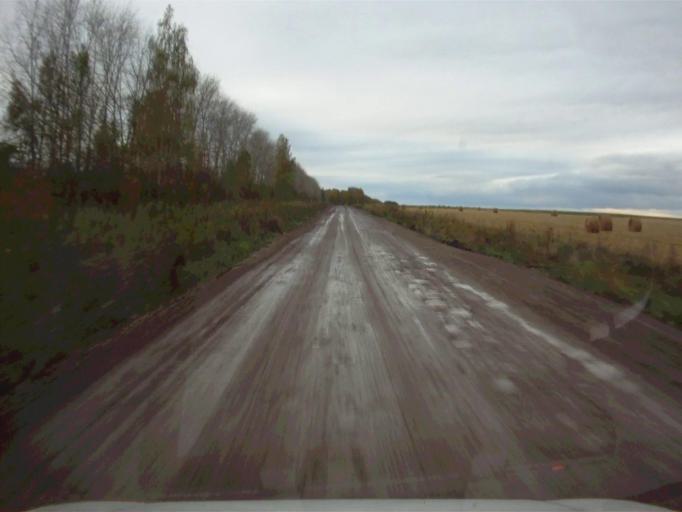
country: RU
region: Sverdlovsk
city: Mikhaylovsk
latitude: 56.1648
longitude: 59.2378
